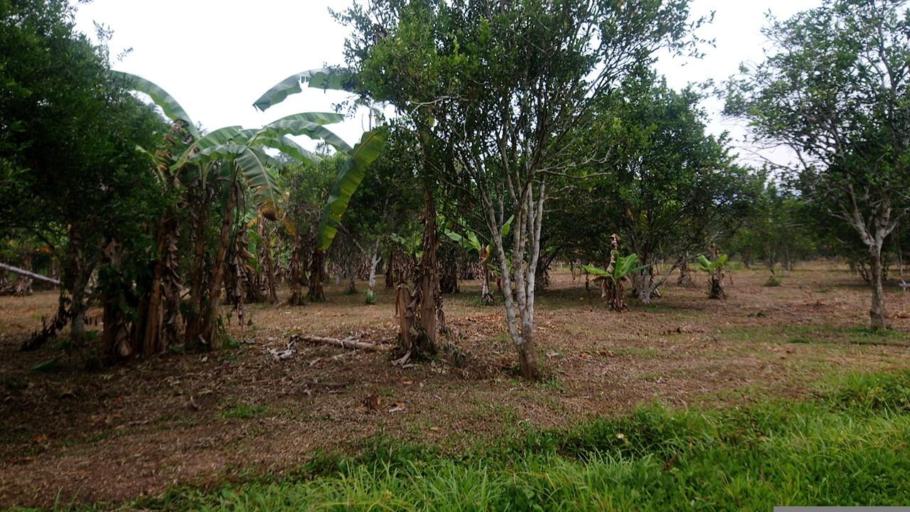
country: BO
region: La Paz
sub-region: Provincia Larecaja
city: Guanay
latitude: -15.5638
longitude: -67.3172
